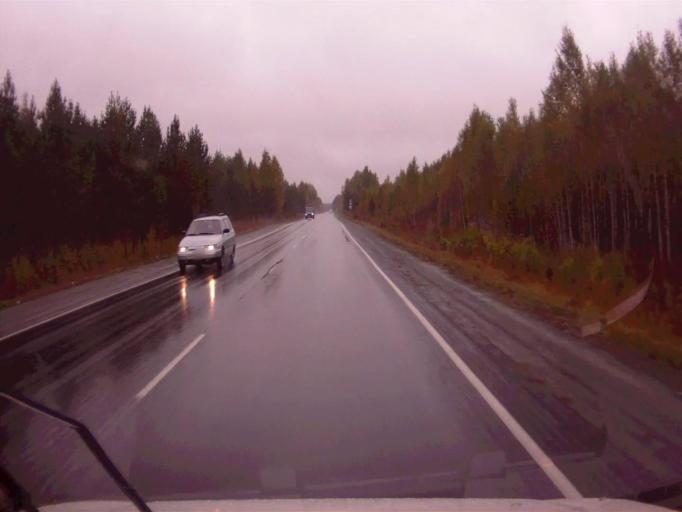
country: RU
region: Chelyabinsk
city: Tayginka
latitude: 55.5394
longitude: 60.6466
